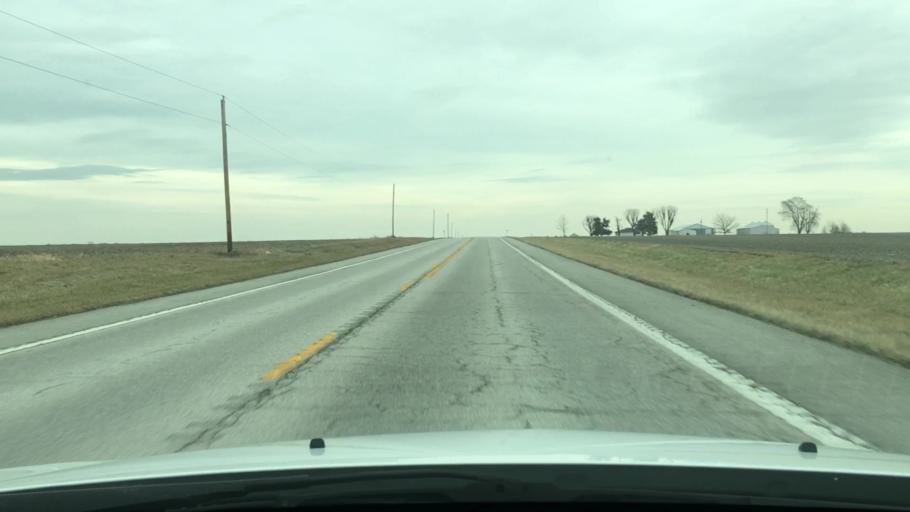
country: US
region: Missouri
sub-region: Audrain County
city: Vandalia
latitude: 39.2802
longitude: -91.6130
